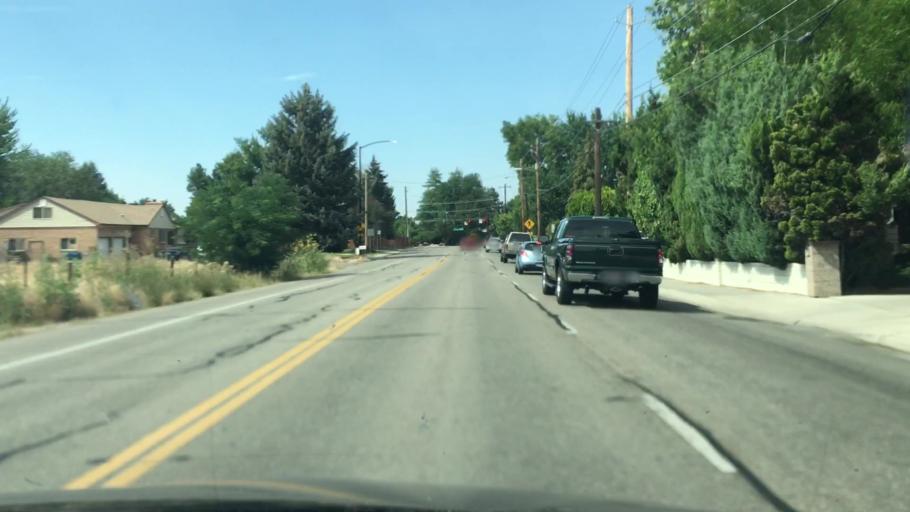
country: US
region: Idaho
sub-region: Ada County
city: Garden City
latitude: 43.6408
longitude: -116.2743
